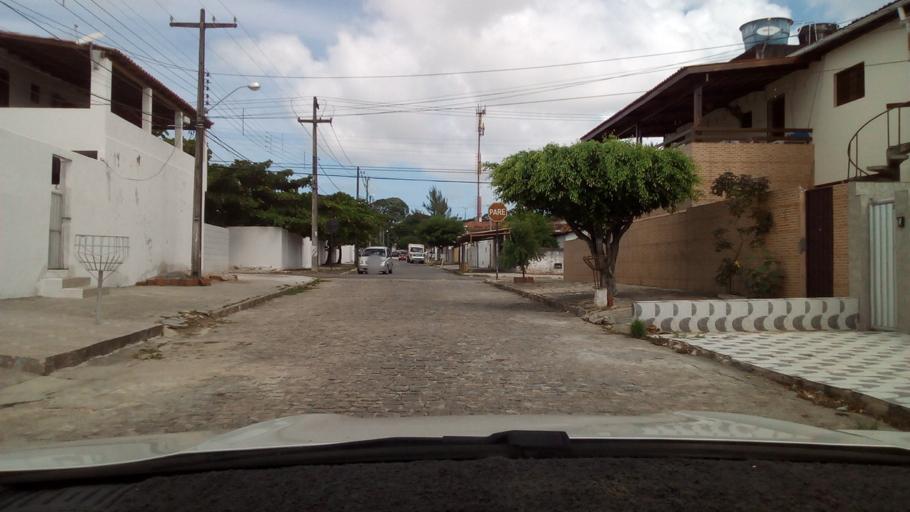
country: BR
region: Paraiba
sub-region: Joao Pessoa
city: Joao Pessoa
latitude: -7.1361
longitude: -34.8529
